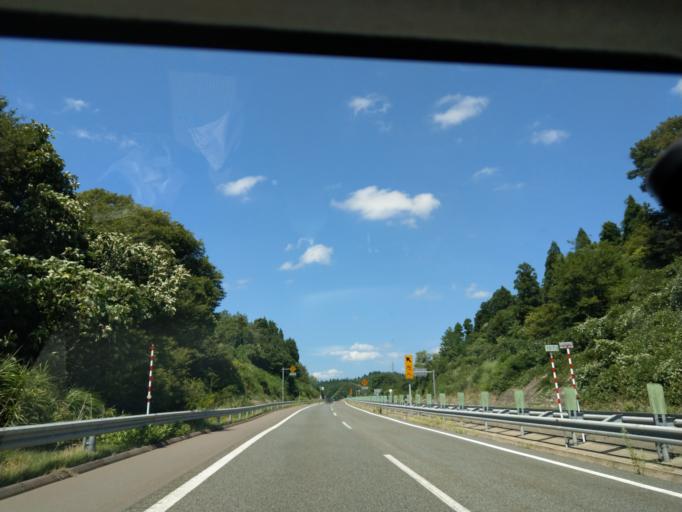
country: JP
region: Akita
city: Akita
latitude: 39.6648
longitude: 140.1886
